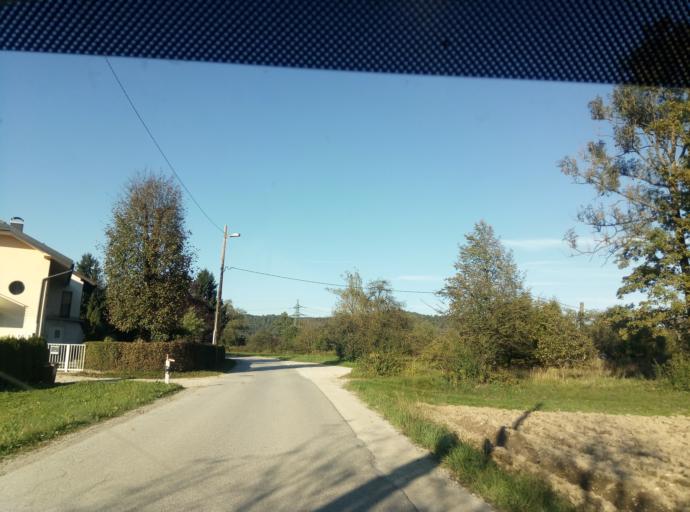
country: SI
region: Ljubljana
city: Ljubljana
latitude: 46.0998
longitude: 14.5025
